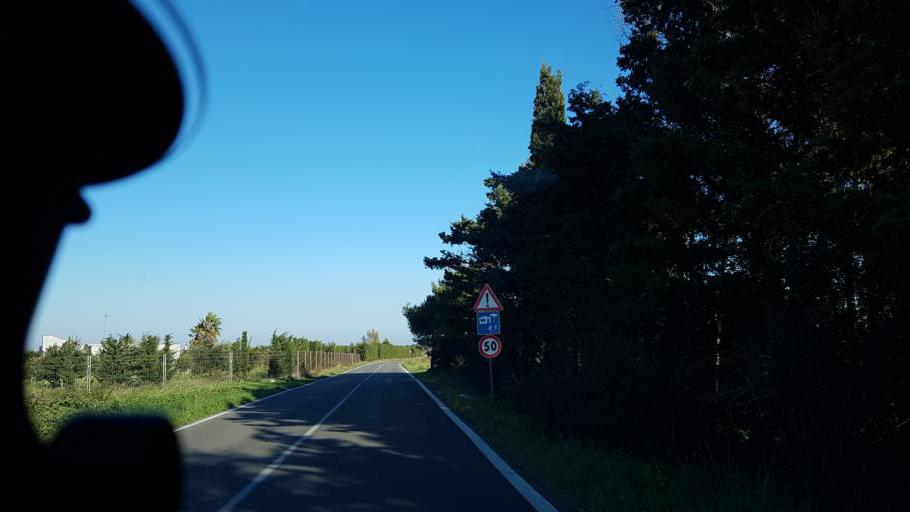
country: IT
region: Apulia
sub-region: Provincia di Lecce
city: Struda
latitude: 40.3927
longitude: 18.2799
